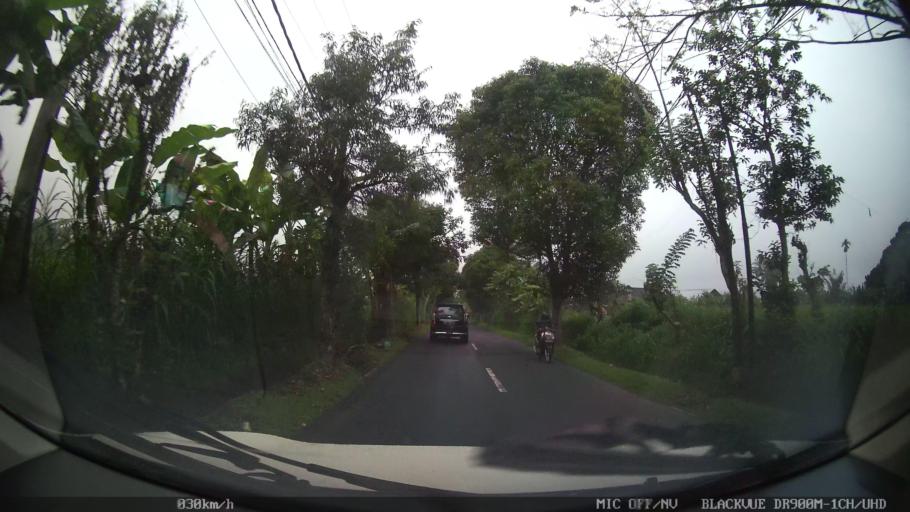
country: ID
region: Bali
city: Banjar Taro Kelod
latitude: -8.3746
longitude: 115.2680
